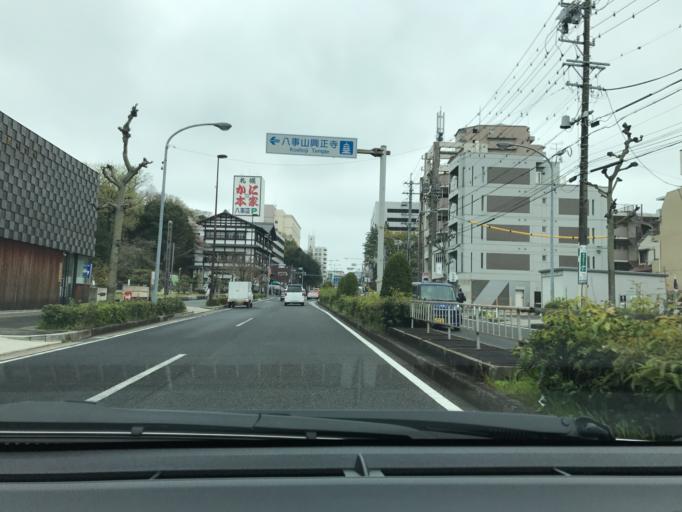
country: JP
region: Aichi
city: Nagoya-shi
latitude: 35.1393
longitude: 136.9609
